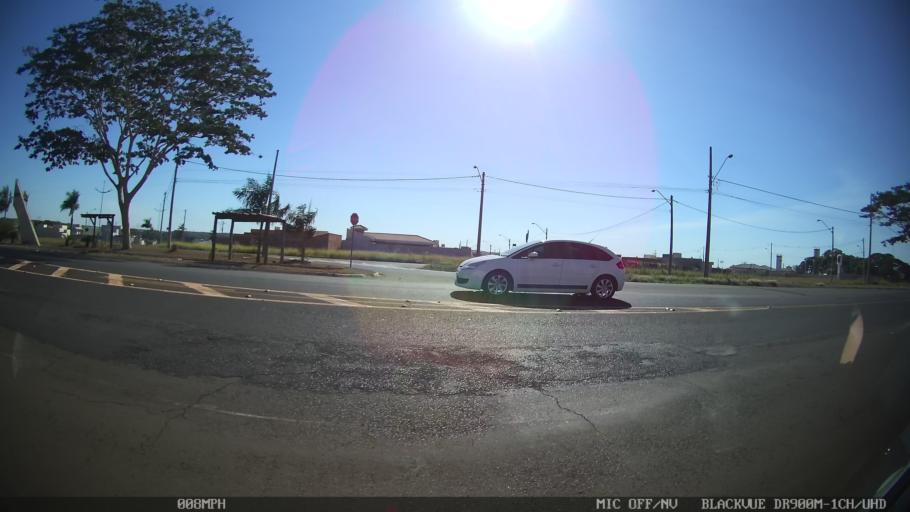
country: BR
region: Sao Paulo
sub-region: Olimpia
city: Olimpia
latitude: -20.7566
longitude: -48.9136
